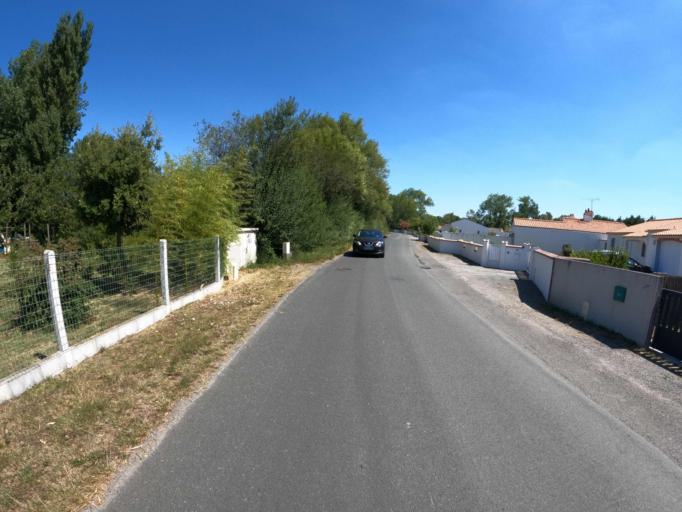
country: FR
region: Pays de la Loire
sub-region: Departement de la Vendee
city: Saint-Jean-de-Monts
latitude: 46.8032
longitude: -2.0841
